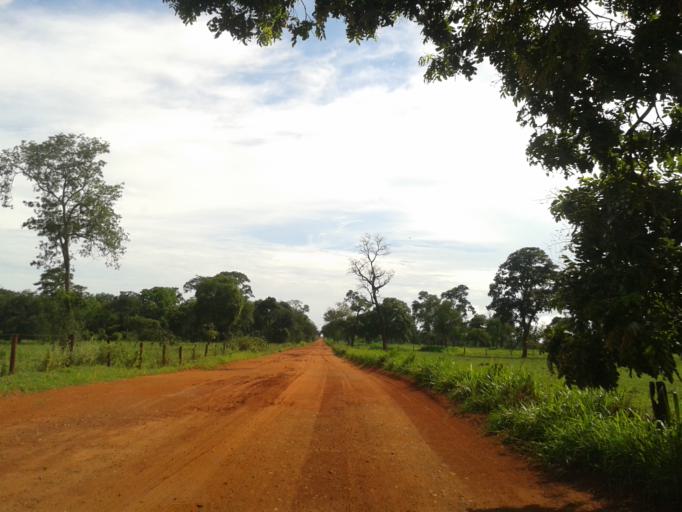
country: BR
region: Minas Gerais
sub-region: Santa Vitoria
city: Santa Vitoria
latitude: -19.1946
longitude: -50.6420
